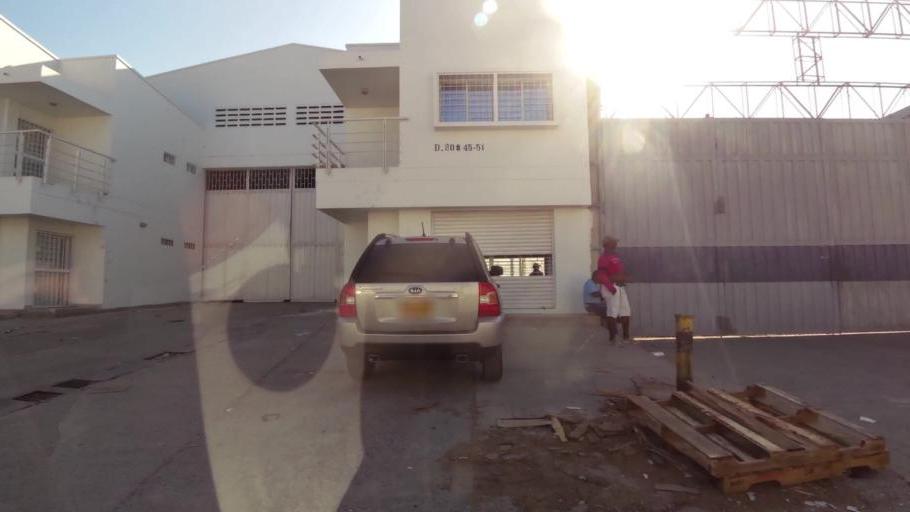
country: CO
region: Bolivar
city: Cartagena
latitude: 10.3991
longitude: -75.5228
